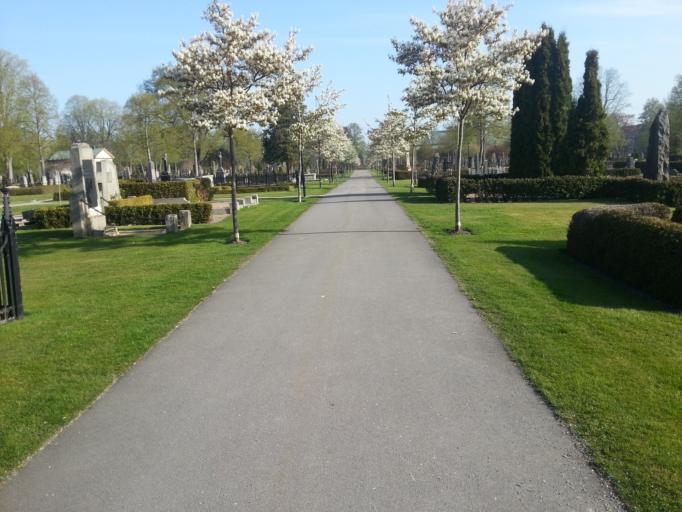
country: SE
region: OEstergoetland
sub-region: Norrkopings Kommun
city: Norrkoping
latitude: 58.5900
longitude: 16.1710
